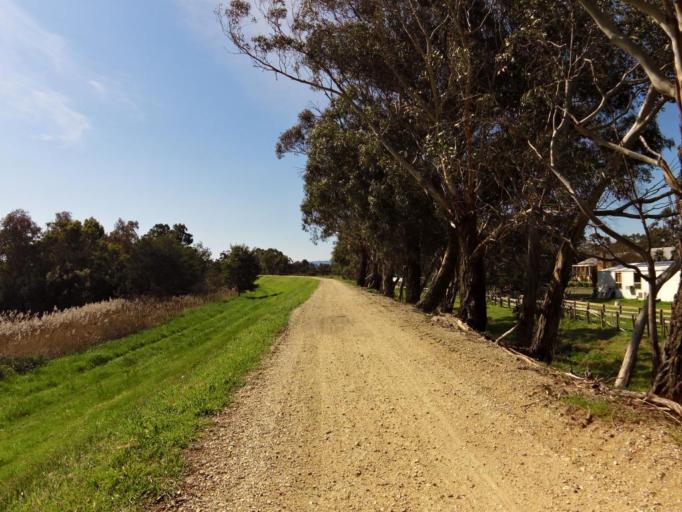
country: AU
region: Victoria
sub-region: Greater Dandenong
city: Keysborough
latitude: -38.0372
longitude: 145.1815
